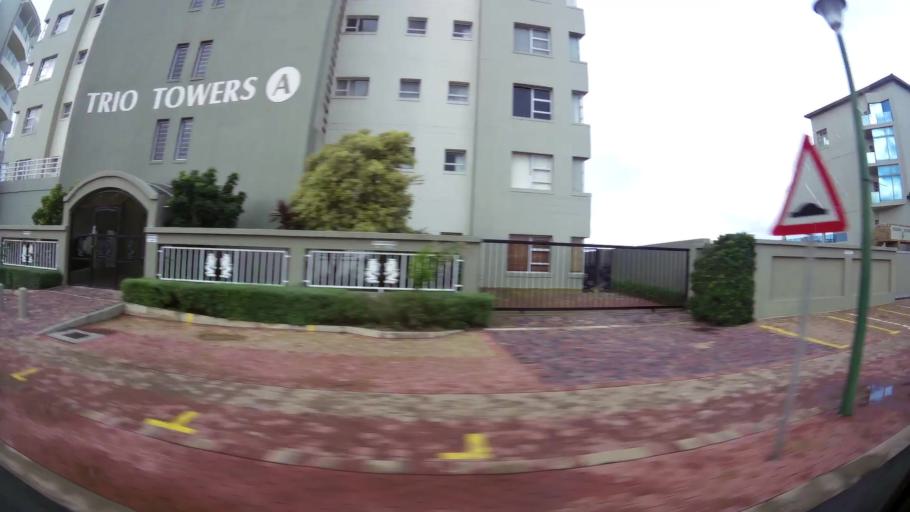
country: ZA
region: Western Cape
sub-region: Eden District Municipality
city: Mossel Bay
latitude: -34.1557
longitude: 22.1092
